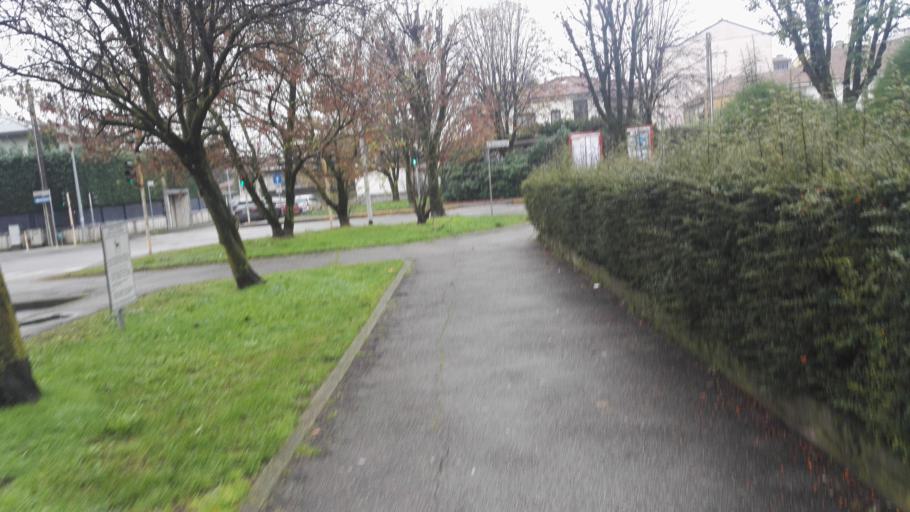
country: IT
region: Lombardy
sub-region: Citta metropolitana di Milano
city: Paullo
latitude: 45.4201
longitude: 9.4049
